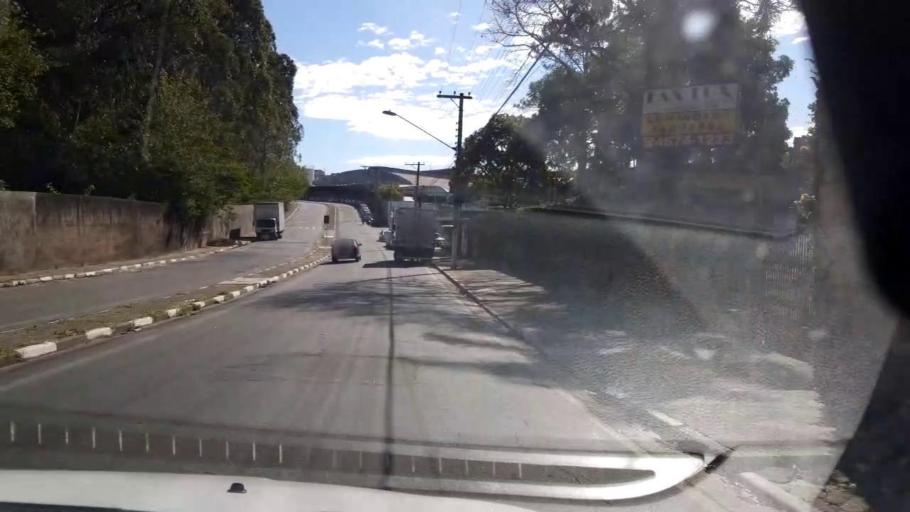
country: BR
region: Sao Paulo
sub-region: Ferraz De Vasconcelos
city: Ferraz de Vasconcelos
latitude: -23.5366
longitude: -46.3868
